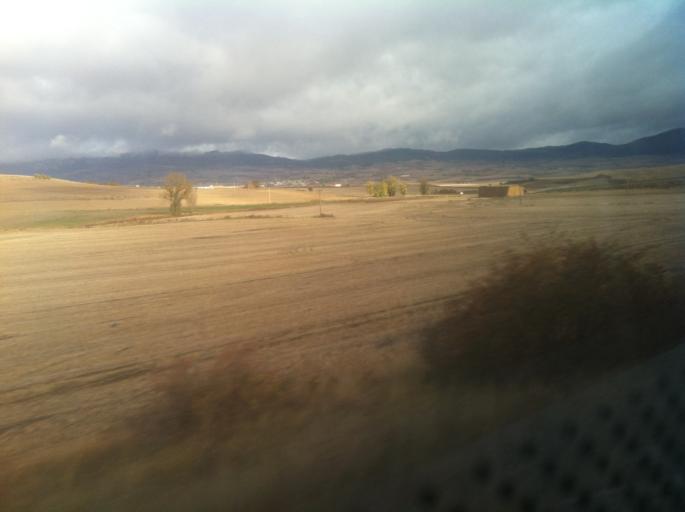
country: ES
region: Castille and Leon
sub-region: Provincia de Burgos
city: Berzosa de Bureba
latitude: 42.6152
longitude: -3.2620
